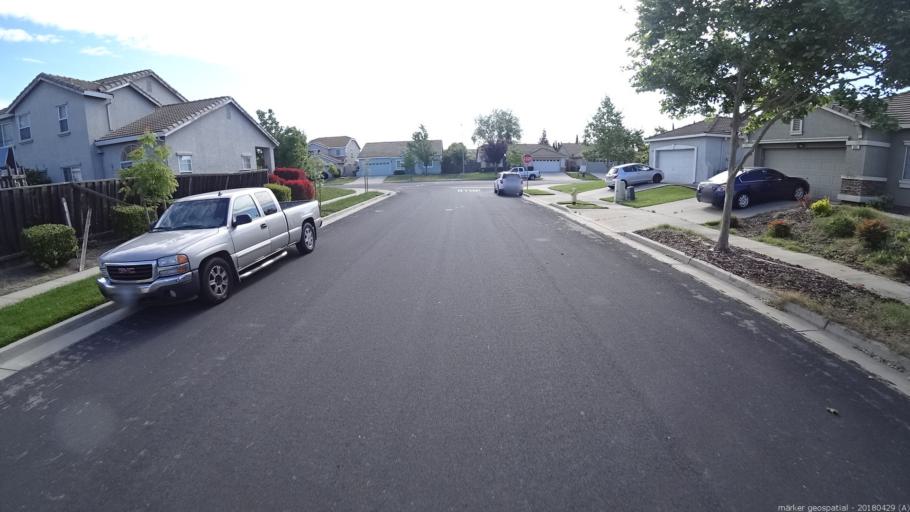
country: US
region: California
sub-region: Yolo County
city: West Sacramento
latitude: 38.5375
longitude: -121.5681
